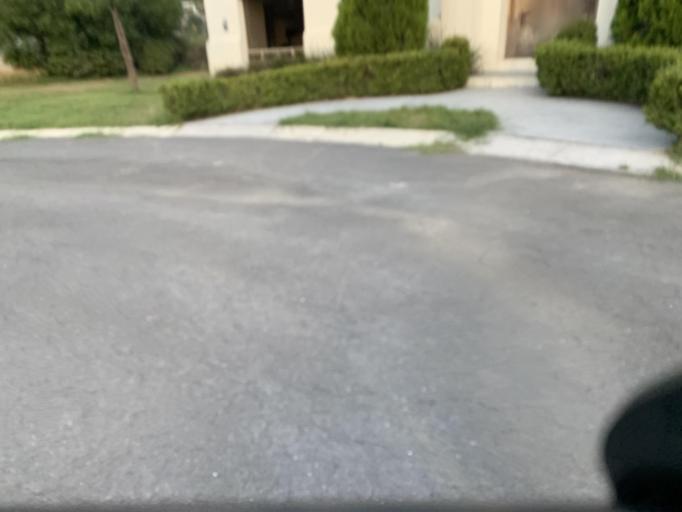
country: MX
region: Nuevo Leon
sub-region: Juarez
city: Bosques de San Pedro
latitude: 25.5196
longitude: -100.1973
